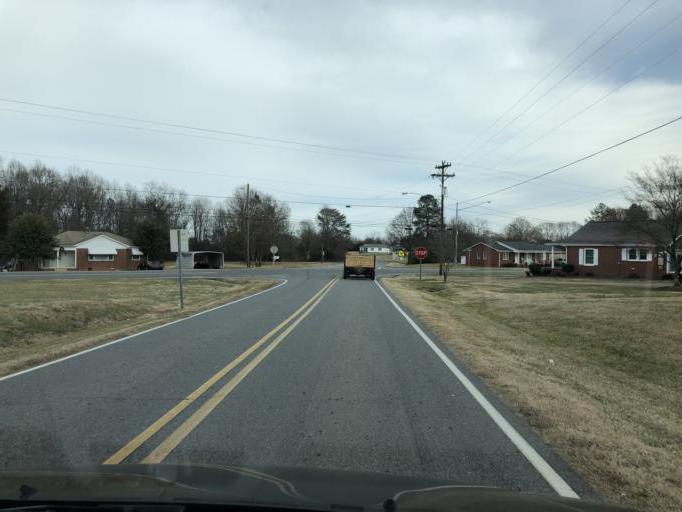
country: US
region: North Carolina
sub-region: Cleveland County
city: Boiling Springs
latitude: 35.2369
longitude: -81.6580
